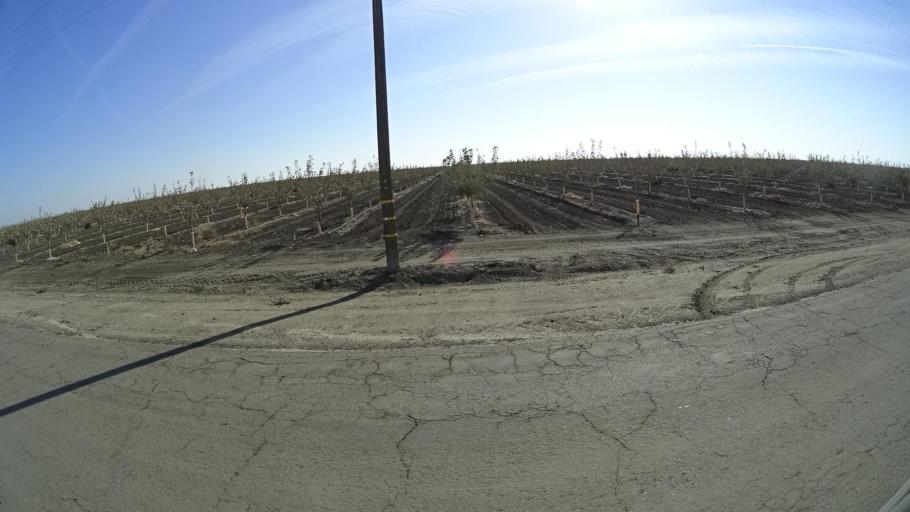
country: US
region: California
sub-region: Kern County
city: Wasco
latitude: 35.7032
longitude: -119.4140
